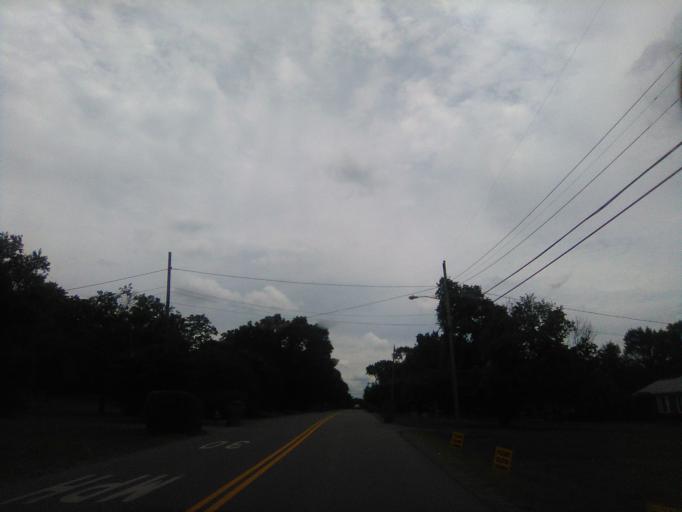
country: US
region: Tennessee
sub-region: Davidson County
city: Belle Meade
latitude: 36.1274
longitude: -86.8923
